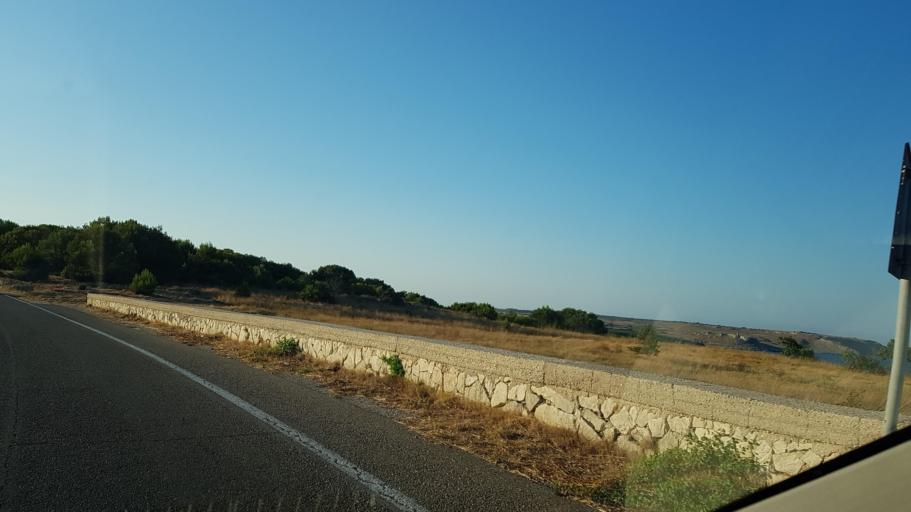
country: IT
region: Apulia
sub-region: Provincia di Lecce
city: Cerfignano
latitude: 40.0674
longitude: 18.4799
